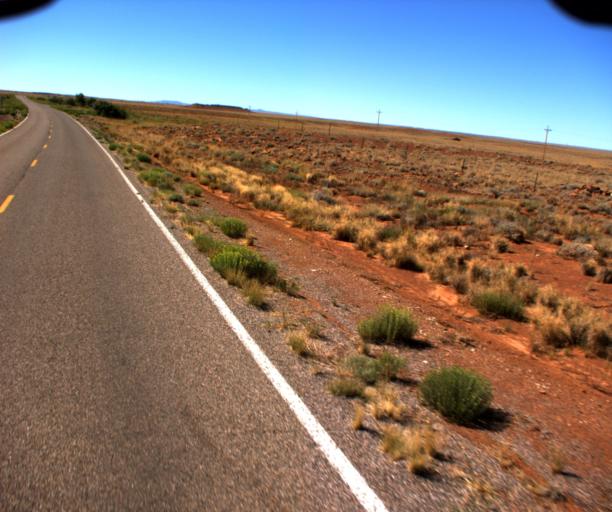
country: US
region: Arizona
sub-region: Coconino County
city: LeChee
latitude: 35.2337
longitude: -110.9581
